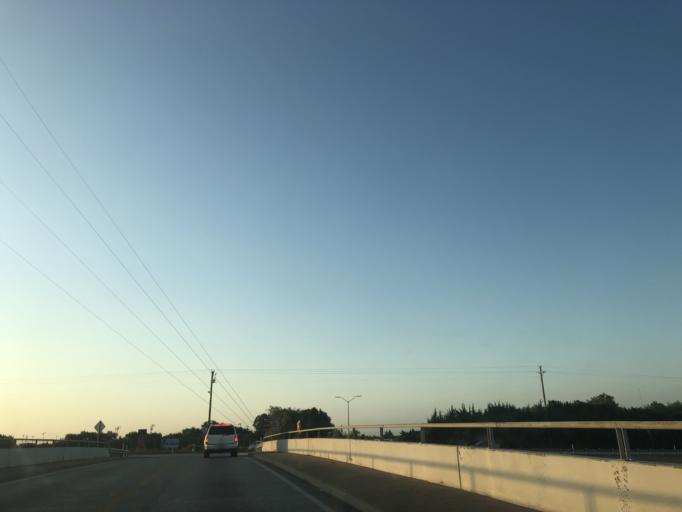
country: US
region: Texas
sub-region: Dallas County
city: Cedar Hill
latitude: 32.5788
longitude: -96.9577
